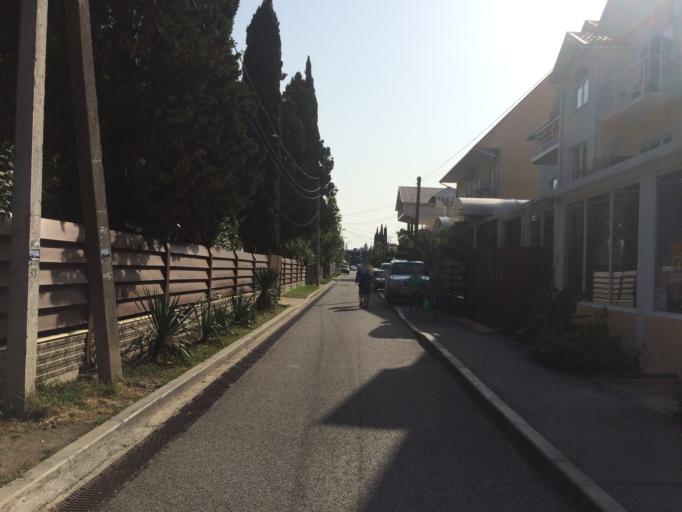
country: RU
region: Krasnodarskiy
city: Adler
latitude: 43.3945
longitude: 39.9827
